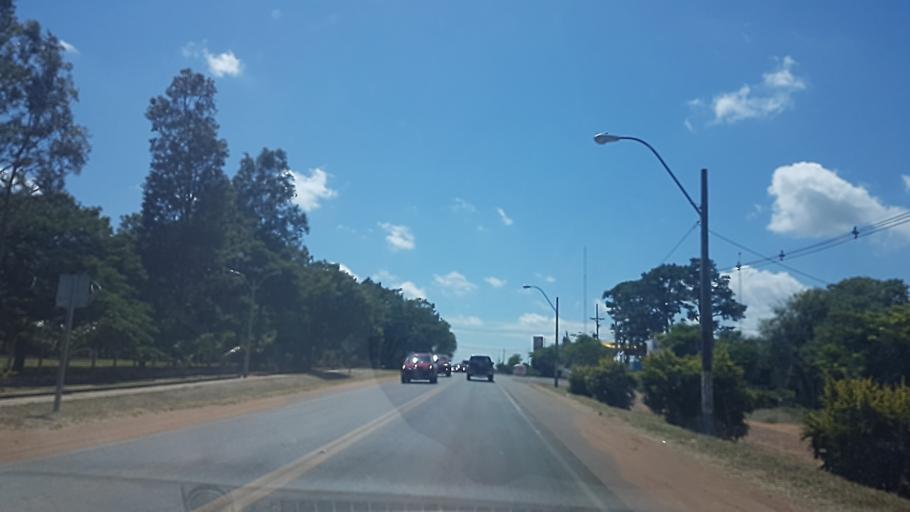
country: PY
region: Misiones
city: San Juan Bautista
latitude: -26.6713
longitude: -57.1335
